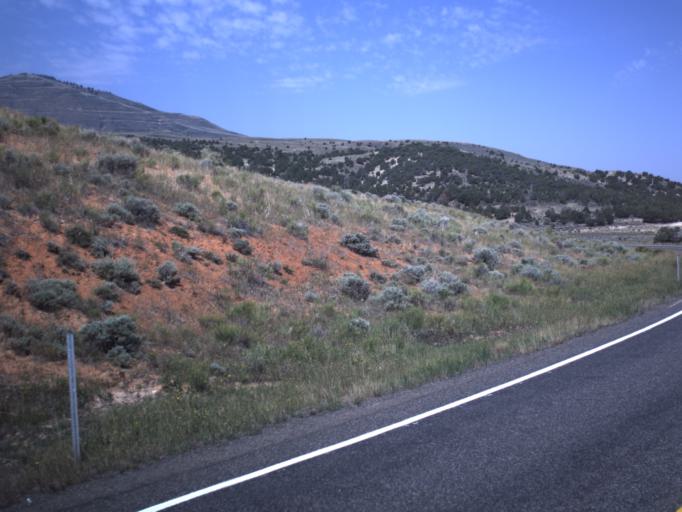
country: US
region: Utah
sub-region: Daggett County
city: Manila
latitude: 40.9819
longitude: -109.8379
